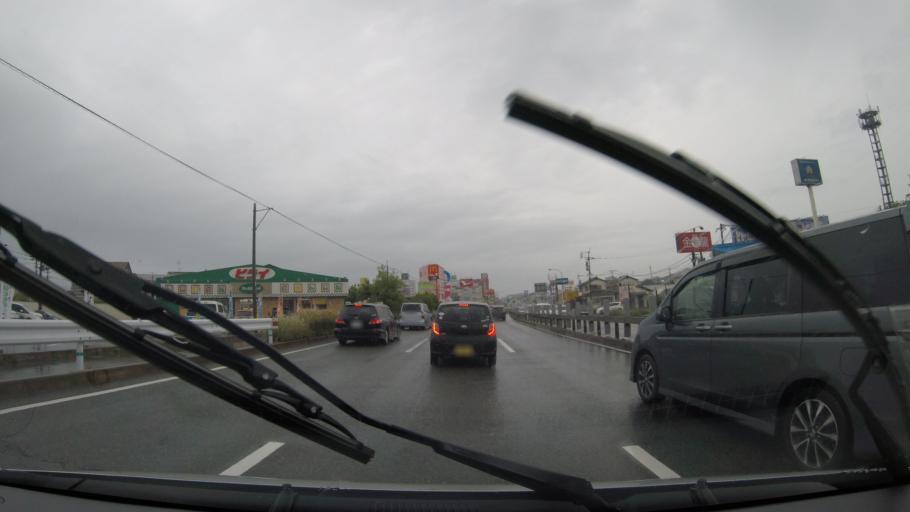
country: JP
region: Fukuoka
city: Shingu
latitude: 33.6973
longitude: 130.4510
